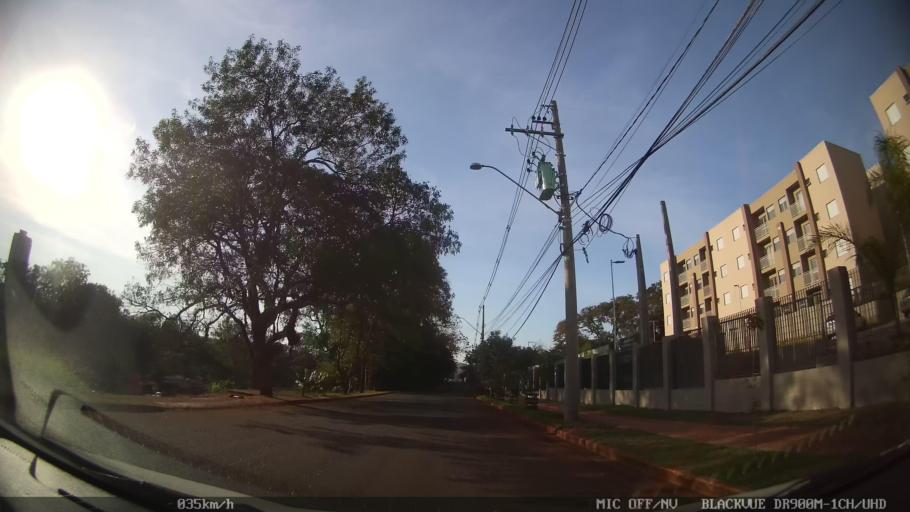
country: BR
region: Sao Paulo
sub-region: Ribeirao Preto
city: Ribeirao Preto
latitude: -21.2714
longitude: -47.8160
